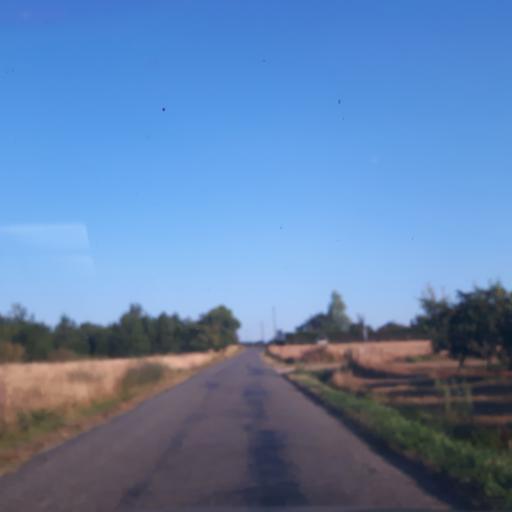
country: FR
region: Midi-Pyrenees
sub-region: Departement de la Haute-Garonne
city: Villaudric
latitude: 43.8028
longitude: 1.4428
